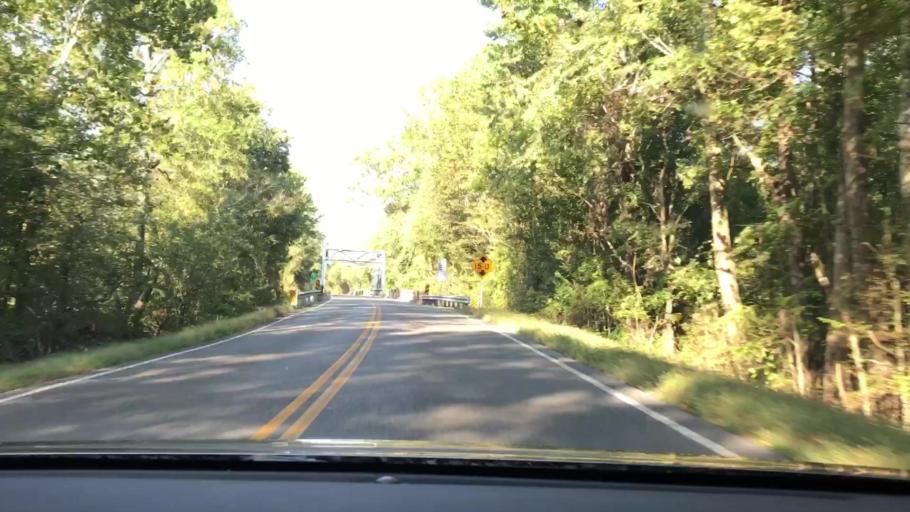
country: US
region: Kentucky
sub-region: Marshall County
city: Benton
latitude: 36.7685
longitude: -88.2765
